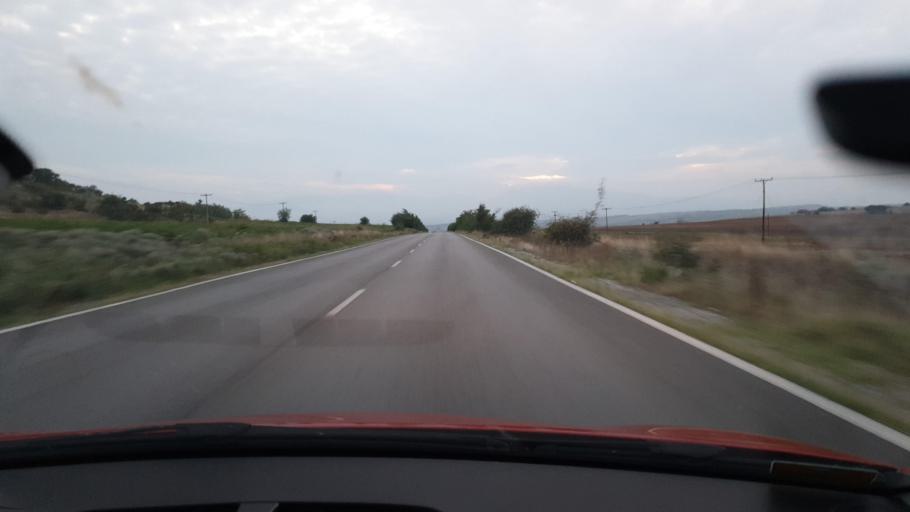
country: GR
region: Central Macedonia
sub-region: Nomos Kilkis
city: Polykastro
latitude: 41.0140
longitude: 22.6457
